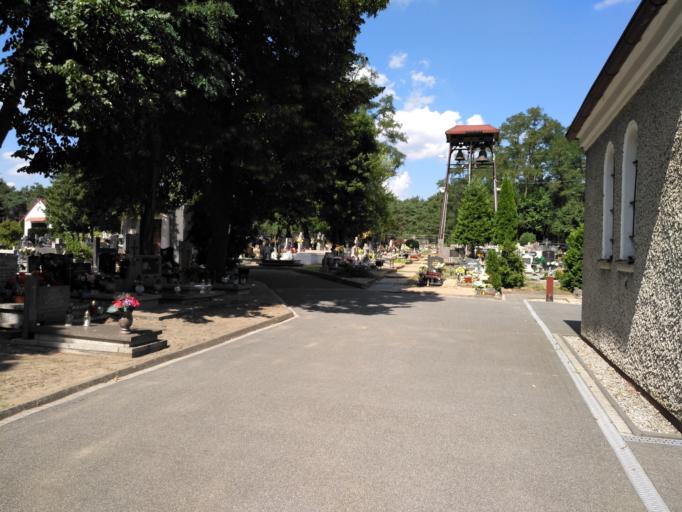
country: PL
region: Kujawsko-Pomorskie
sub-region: Powiat bydgoski
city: Osielsko
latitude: 53.1280
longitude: 18.1002
